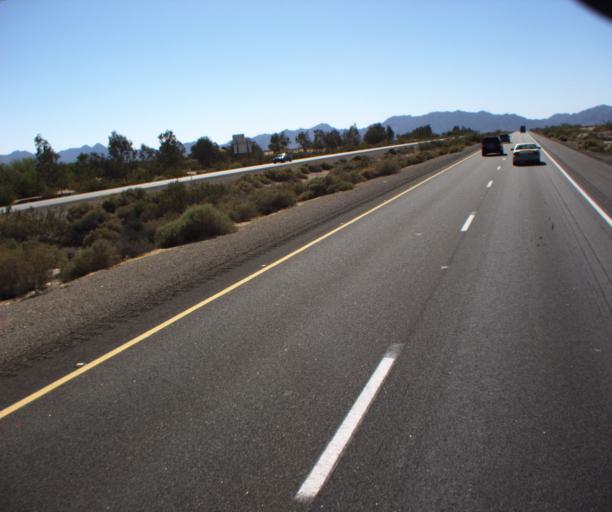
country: US
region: Arizona
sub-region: Yuma County
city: Wellton
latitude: 32.6568
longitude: -114.1643
